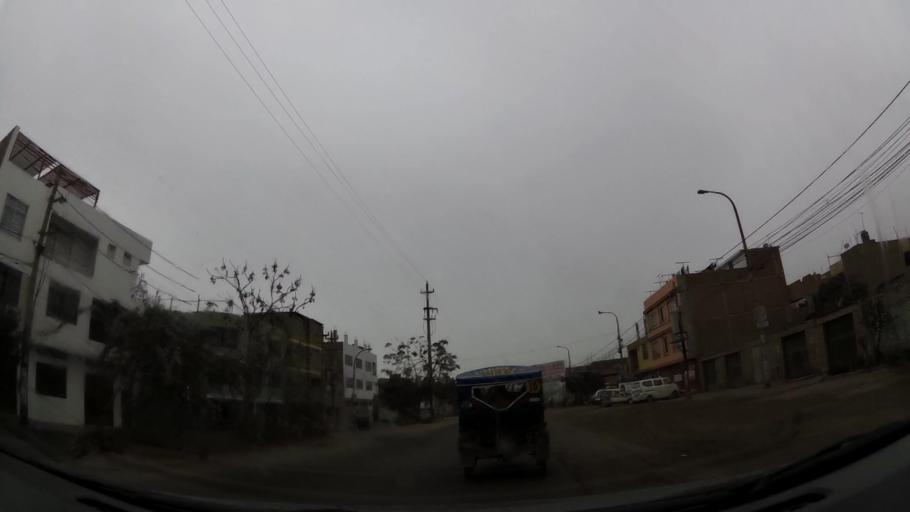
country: PE
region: Lima
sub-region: Lima
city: Urb. Santo Domingo
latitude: -11.8797
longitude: -77.0745
